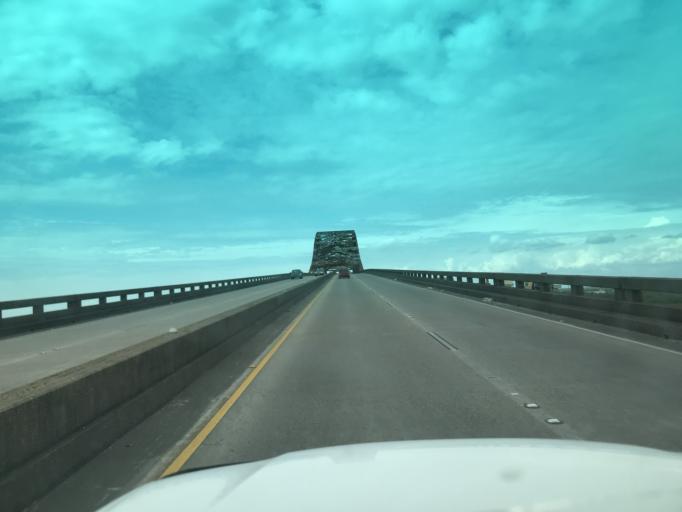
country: US
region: Louisiana
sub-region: Saint Bernard Parish
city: Chalmette
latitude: 30.0018
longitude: -89.9387
